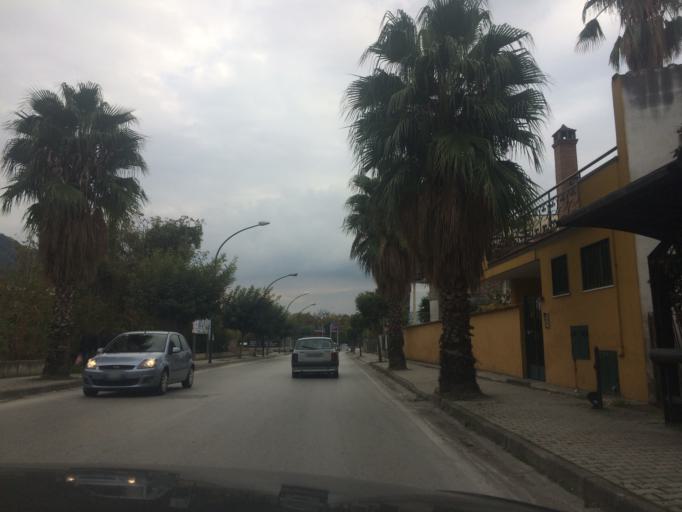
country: IT
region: Campania
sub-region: Provincia di Napoli
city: Palma Campania
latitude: 40.8677
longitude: 14.5479
